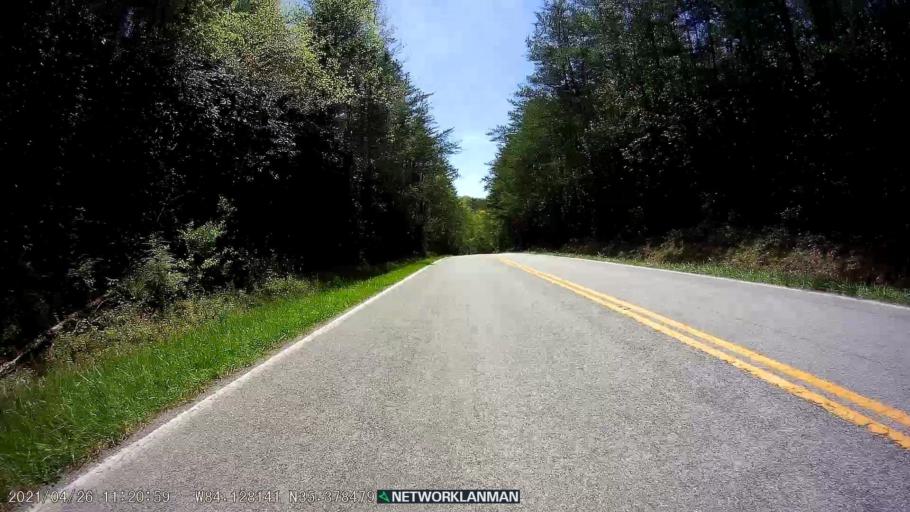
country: US
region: Tennessee
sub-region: Monroe County
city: Vonore
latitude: 35.3786
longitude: -84.1280
